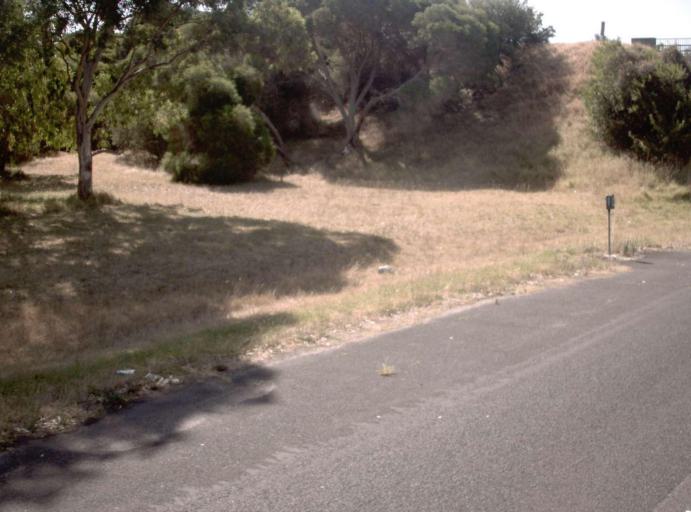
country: AU
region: Victoria
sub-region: Kingston
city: Patterson Lakes
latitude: -38.0675
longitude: 145.1499
